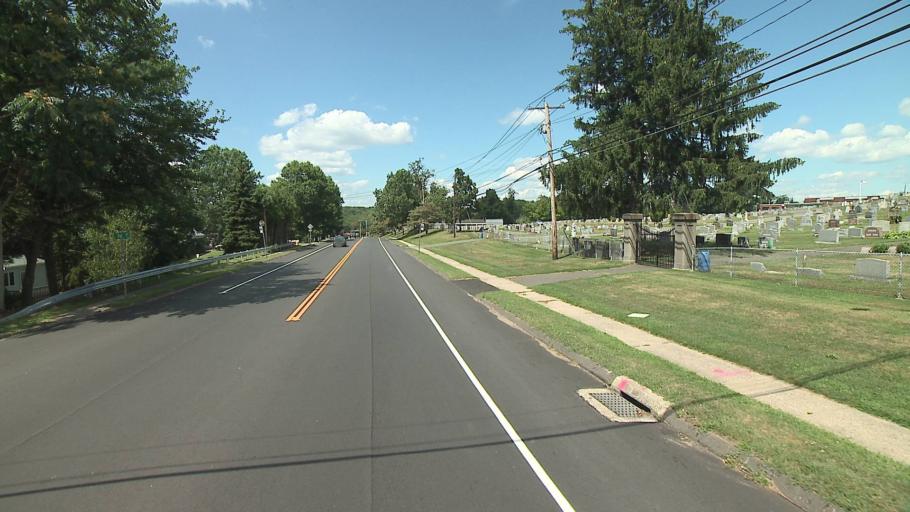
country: US
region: Connecticut
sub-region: Fairfield County
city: Stratford
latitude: 41.2281
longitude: -73.1529
